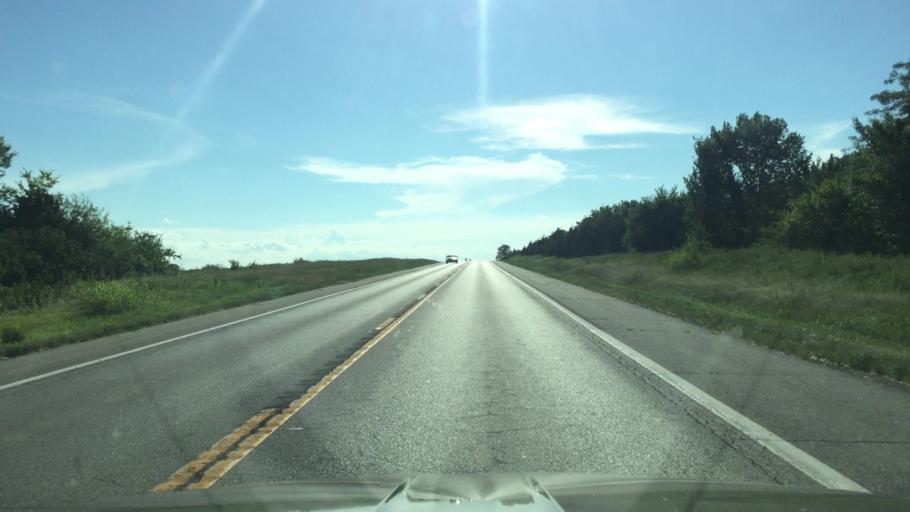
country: US
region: Missouri
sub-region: Pettis County
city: Sedalia
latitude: 38.6941
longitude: -93.1060
